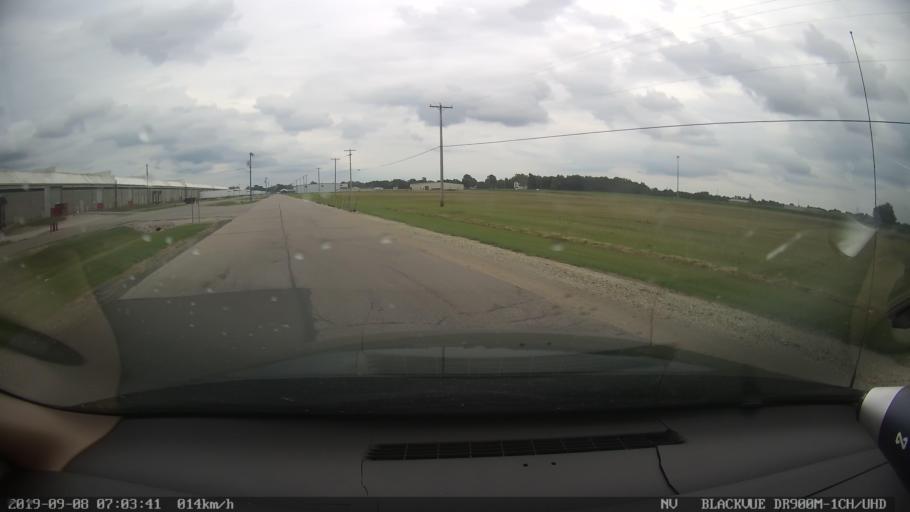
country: US
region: Ohio
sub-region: Richland County
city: Shelby
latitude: 40.8968
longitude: -82.6755
